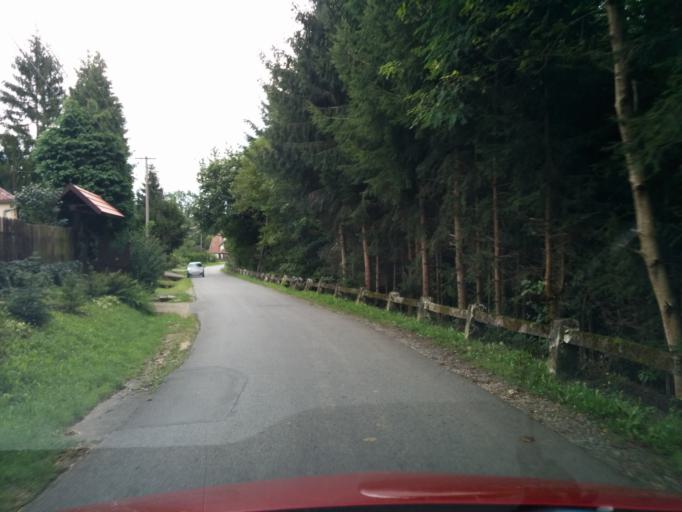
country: AT
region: Burgenland
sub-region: Politischer Bezirk Oberwart
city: Rechnitz
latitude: 47.3472
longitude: 16.4873
